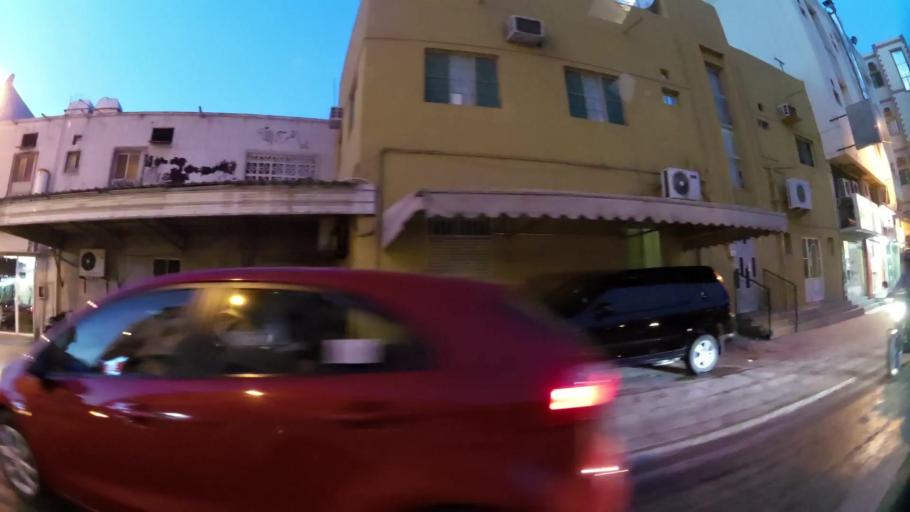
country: BH
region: Manama
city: Jidd Hafs
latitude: 26.2050
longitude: 50.5517
